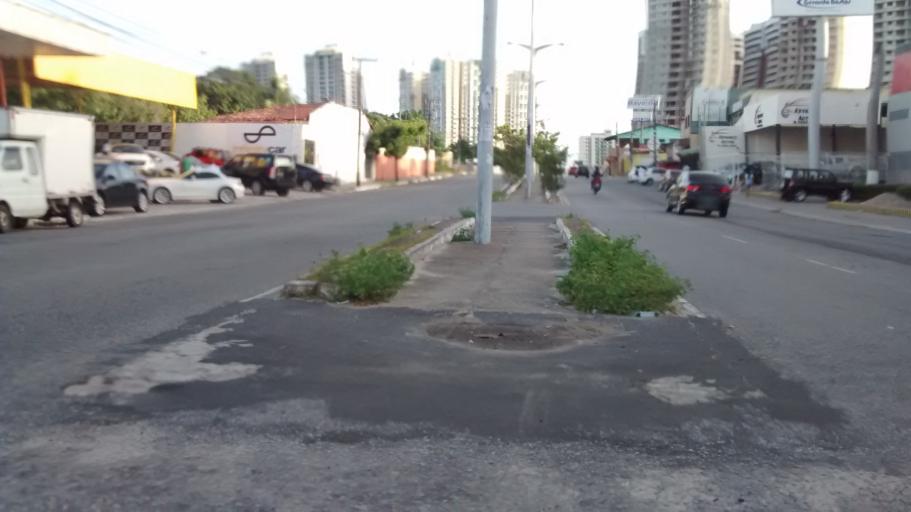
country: BR
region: Ceara
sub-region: Fortaleza
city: Fortaleza
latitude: -3.7618
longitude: -38.4934
